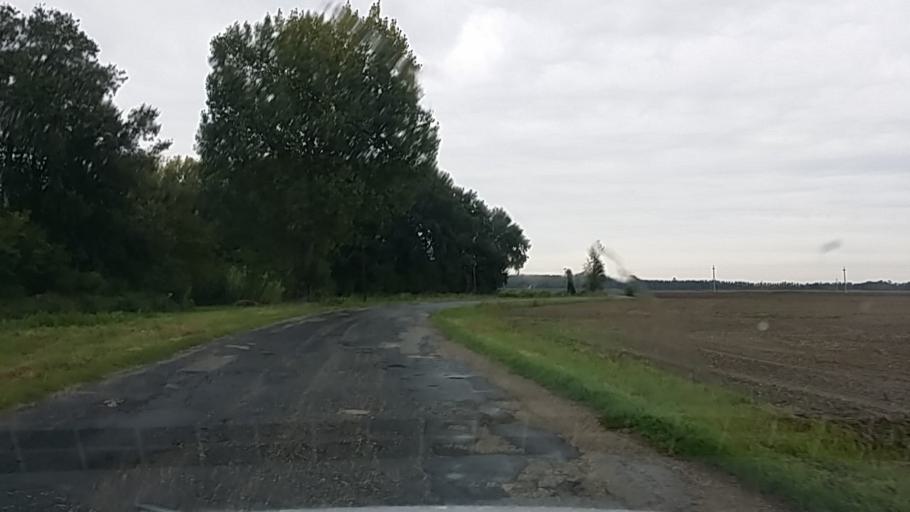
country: HU
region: Pest
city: Domsod
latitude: 47.0780
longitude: 18.9859
